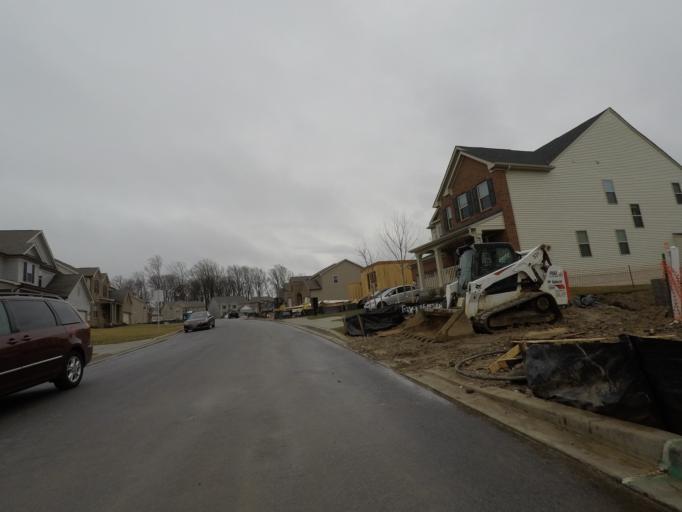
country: US
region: Maryland
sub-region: Howard County
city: Ellicott City
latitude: 39.3050
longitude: -76.8202
